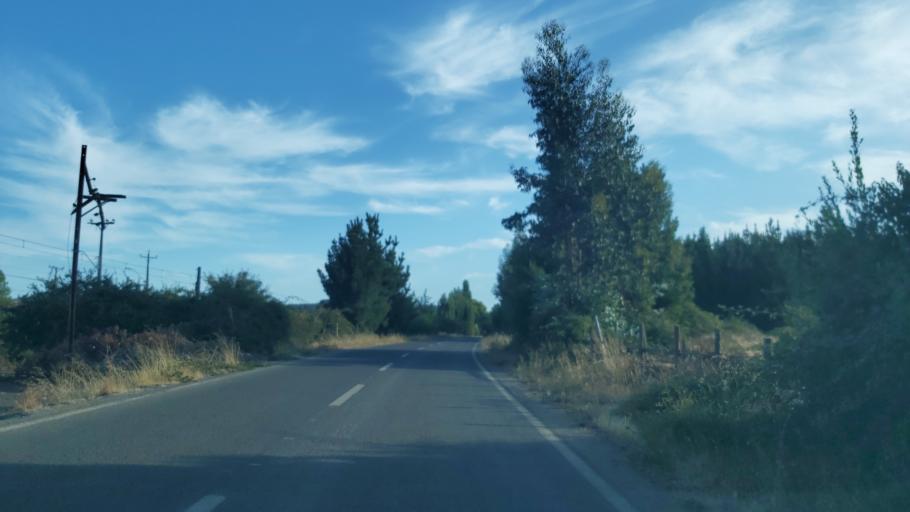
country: CL
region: Biobio
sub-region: Provincia de Biobio
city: La Laja
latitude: -37.1562
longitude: -72.9170
